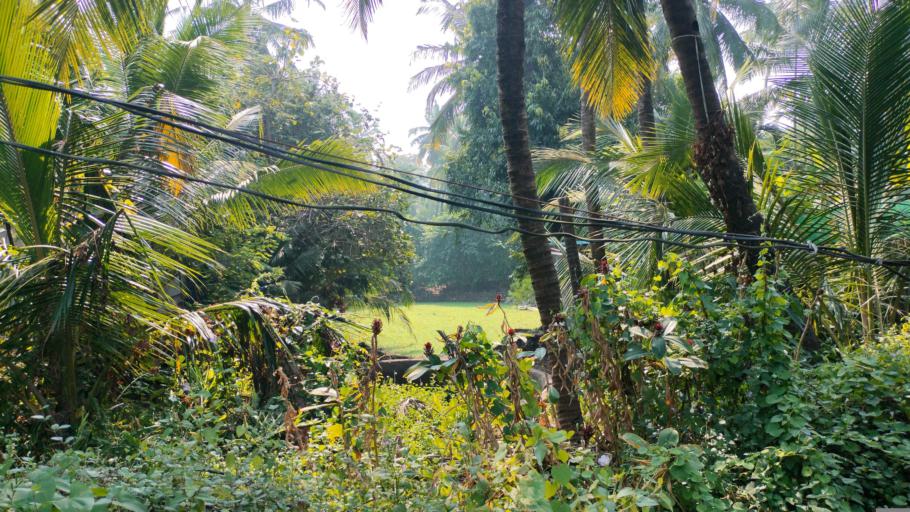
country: IN
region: Maharashtra
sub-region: Thane
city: Virar
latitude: 19.4269
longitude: 72.7804
